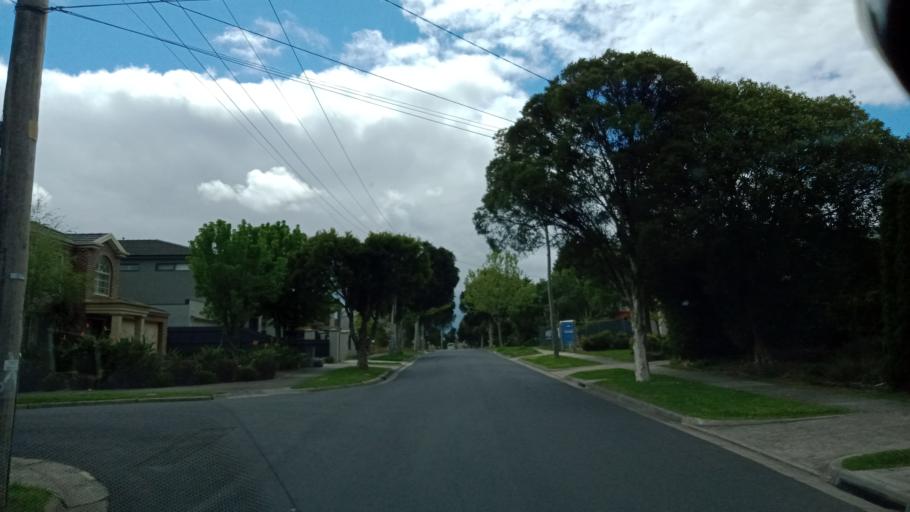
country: AU
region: Victoria
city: Burwood East
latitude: -37.8692
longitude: 145.1555
